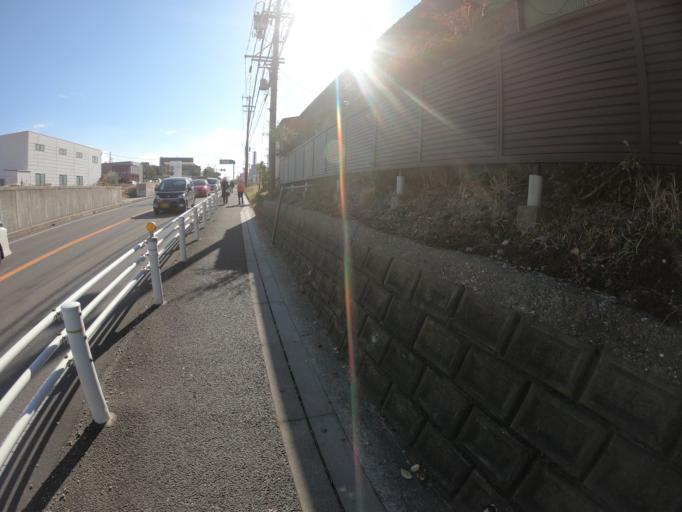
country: JP
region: Aichi
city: Seto
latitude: 35.1304
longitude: 137.0405
